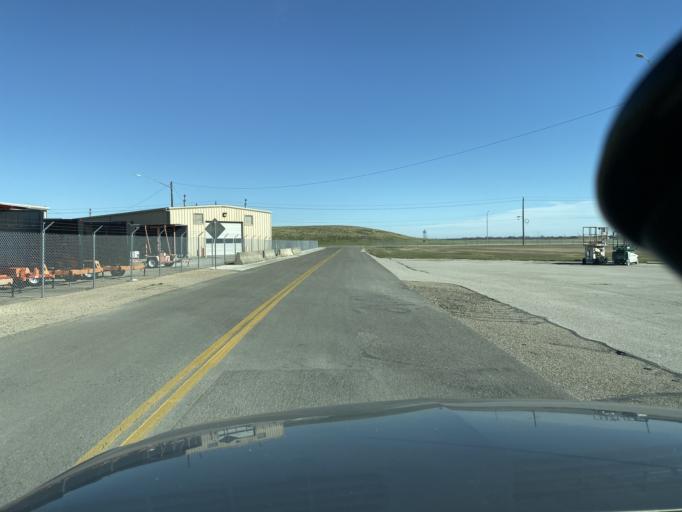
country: US
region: Texas
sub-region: Travis County
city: Hornsby Bend
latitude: 30.1928
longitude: -97.6654
